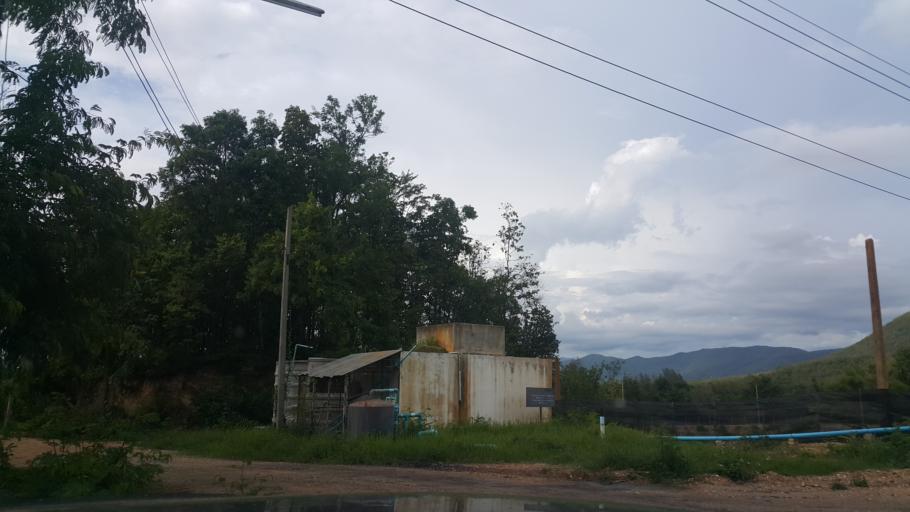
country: TH
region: Chiang Mai
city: Mae On
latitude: 18.7237
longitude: 99.2199
